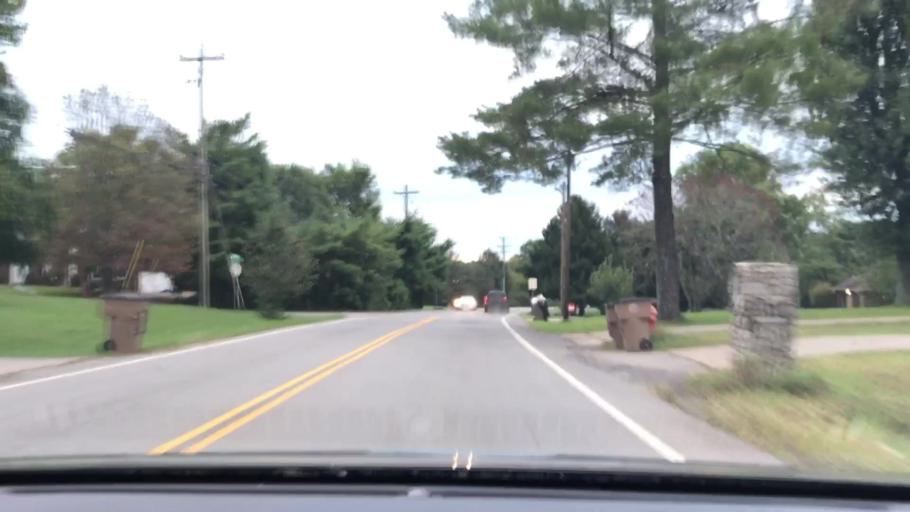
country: US
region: Tennessee
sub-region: Davidson County
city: Oak Hill
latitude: 36.0684
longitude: -86.7091
